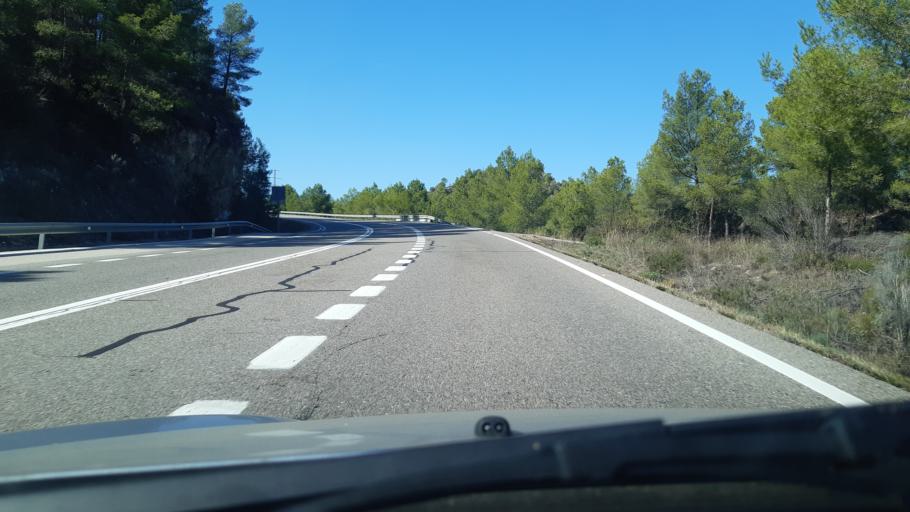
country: ES
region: Catalonia
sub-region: Provincia de Tarragona
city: Rasquera
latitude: 40.9939
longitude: 0.5583
